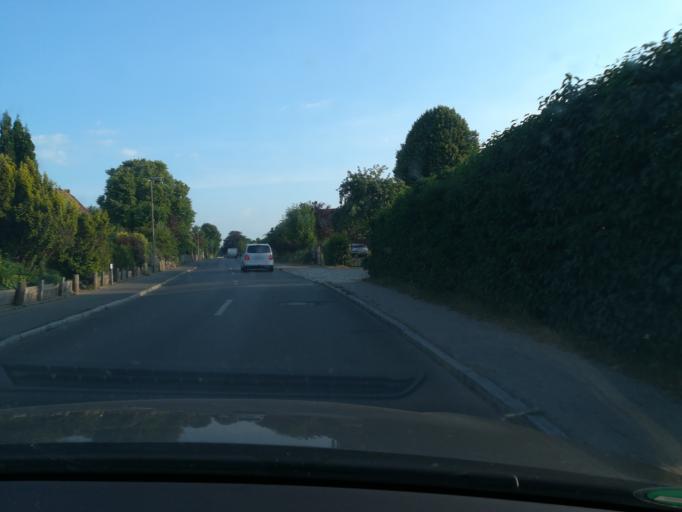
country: DE
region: Schleswig-Holstein
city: Grossensee
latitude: 53.6170
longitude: 10.3411
